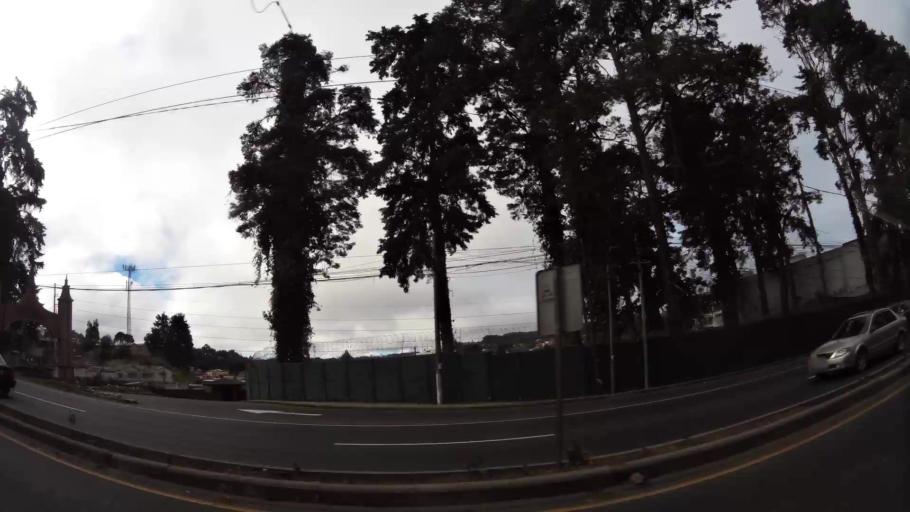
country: GT
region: Guatemala
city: Santa Catarina Pinula
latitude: 14.5575
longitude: -90.4572
